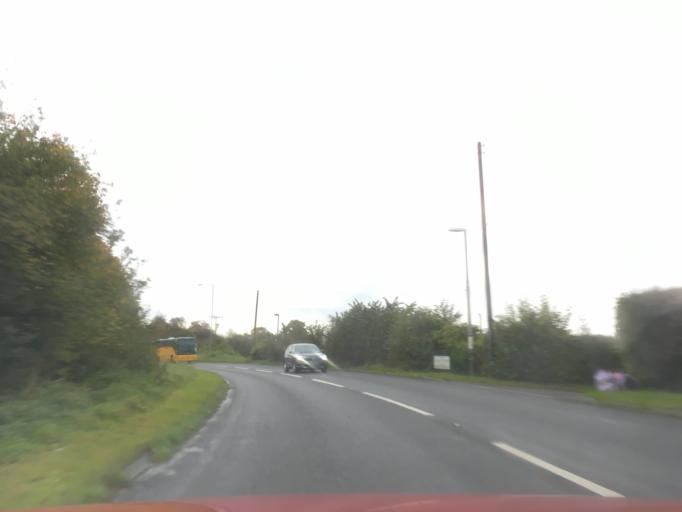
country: GB
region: Wales
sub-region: Monmouthshire
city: Caldicot
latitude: 51.6085
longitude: -2.7157
